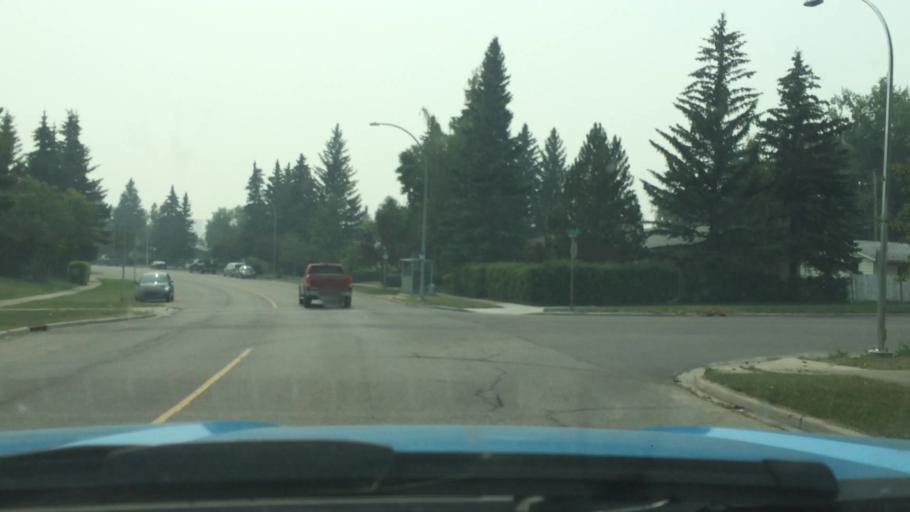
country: CA
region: Alberta
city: Calgary
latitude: 51.1012
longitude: -114.1294
